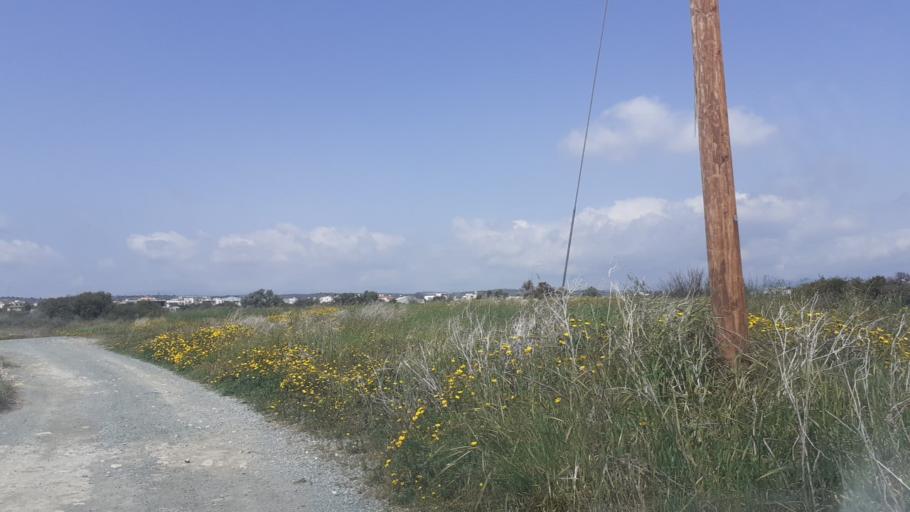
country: CY
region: Limassol
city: Ypsonas
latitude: 34.6859
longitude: 32.9518
